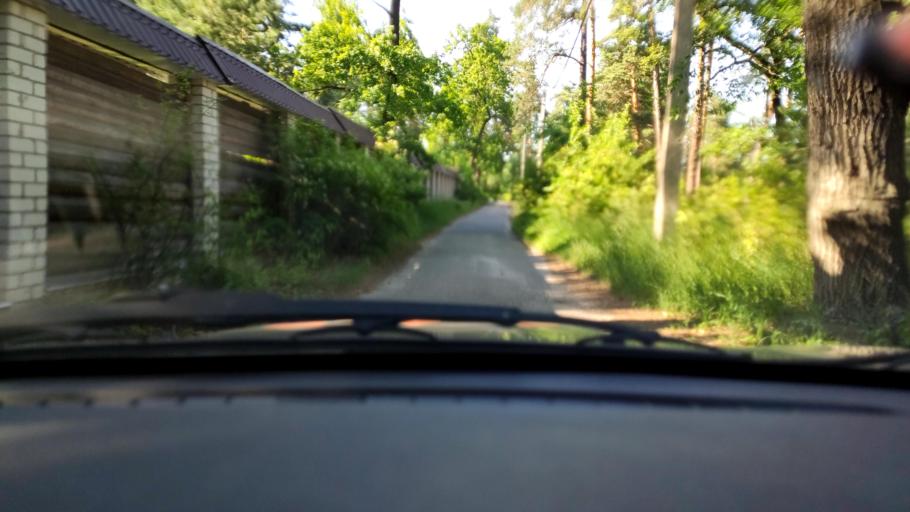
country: RU
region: Voronezj
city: Somovo
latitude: 51.7511
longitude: 39.3744
